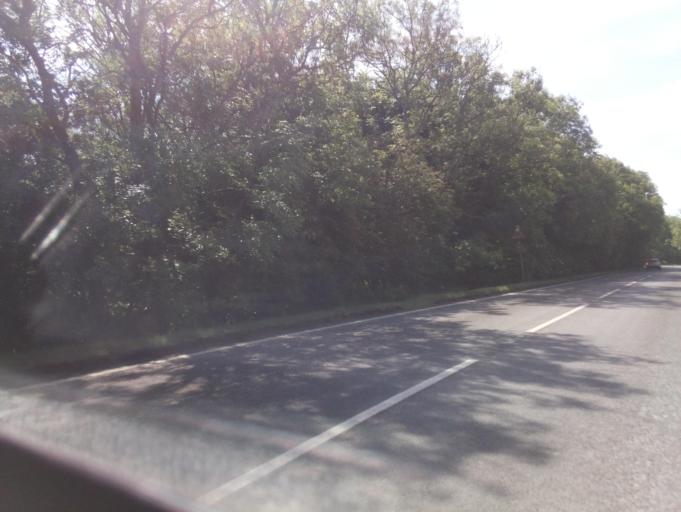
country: GB
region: England
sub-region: North Lincolnshire
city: Manton
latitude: 53.5013
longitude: -0.5823
